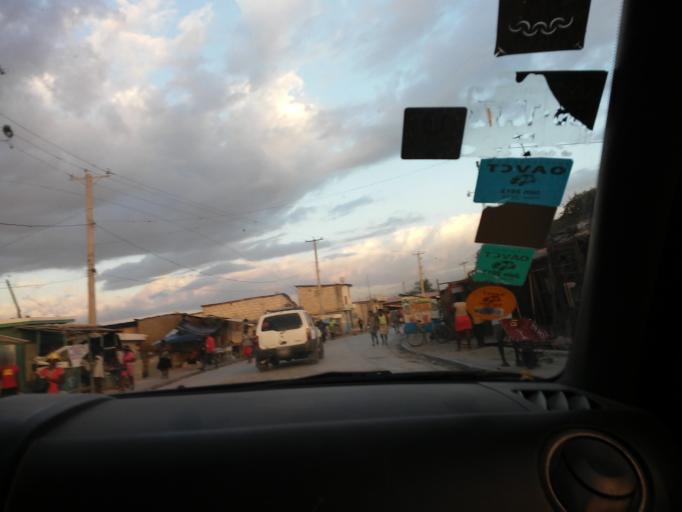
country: HT
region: Ouest
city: Port-au-Prince
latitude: 18.5653
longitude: -72.3467
